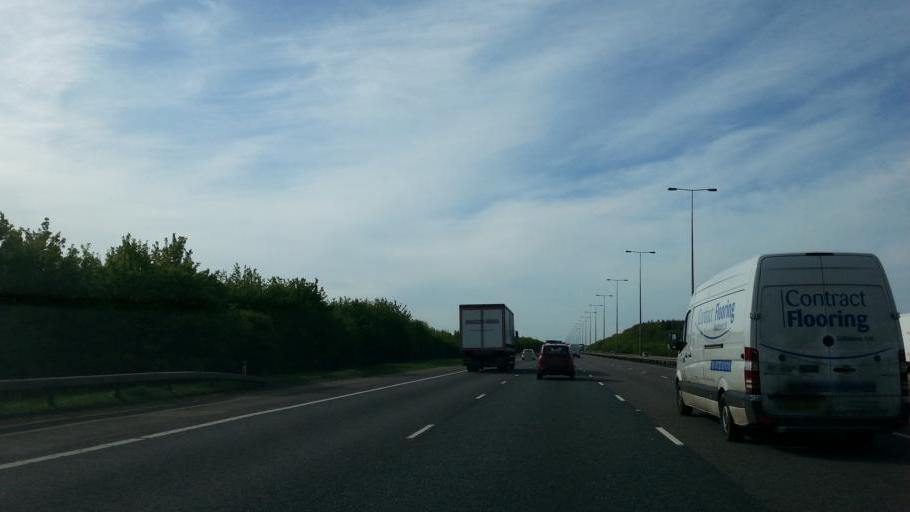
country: GB
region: England
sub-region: Cambridgeshire
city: Sawtry
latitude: 52.4088
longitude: -0.2648
